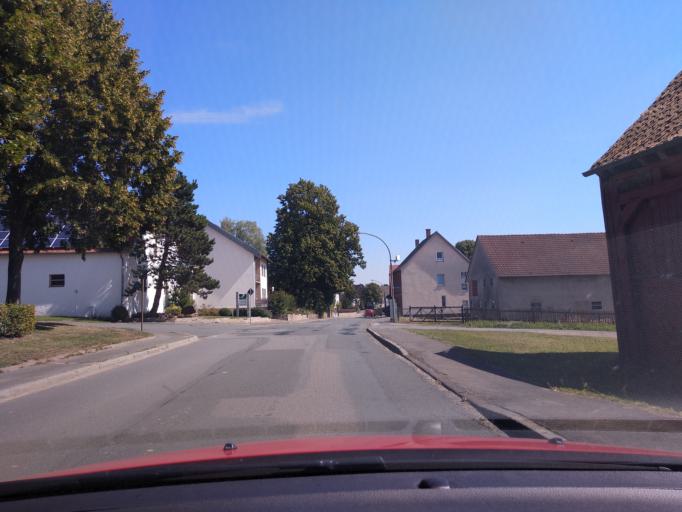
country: DE
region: North Rhine-Westphalia
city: Brakel
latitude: 51.6487
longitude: 9.2103
